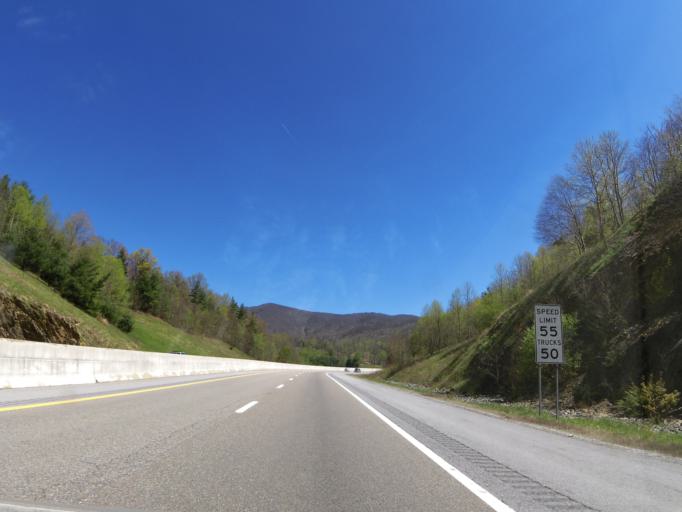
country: US
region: Tennessee
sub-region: Unicoi County
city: Banner Hill
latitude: 36.0051
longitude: -82.5419
